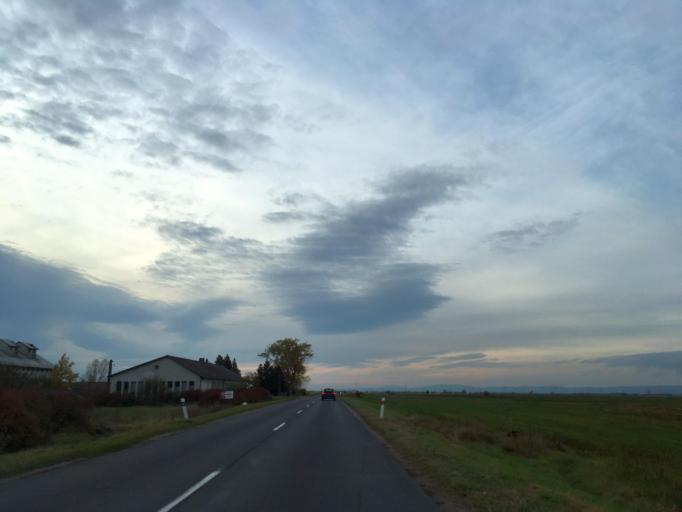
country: SK
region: Trnavsky
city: Samorin
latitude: 48.1037
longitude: 17.3450
